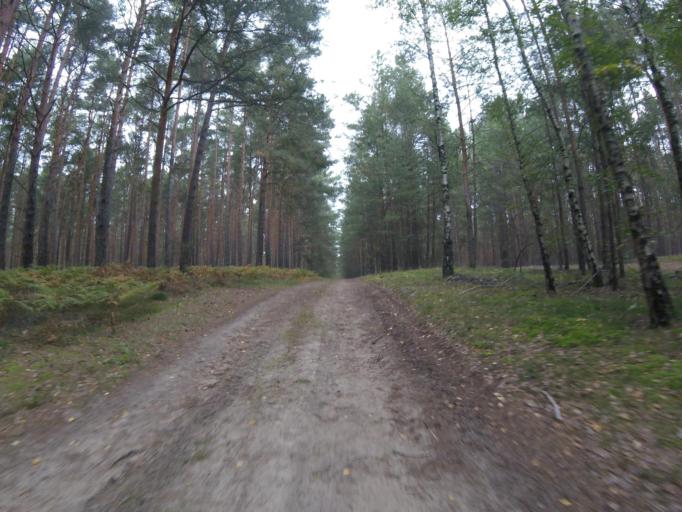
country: DE
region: Brandenburg
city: Gross Koris
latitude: 52.1843
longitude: 13.6765
